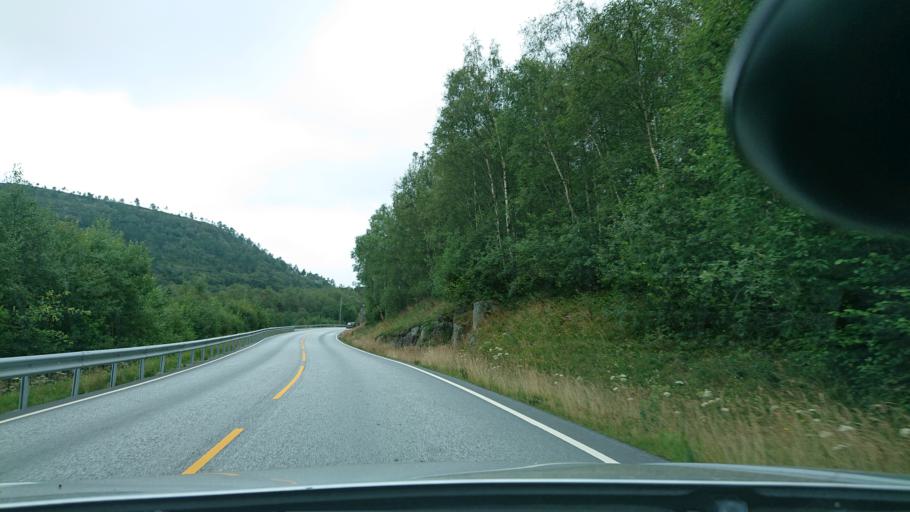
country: NO
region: Rogaland
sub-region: Hjelmeland
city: Hjelmelandsvagen
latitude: 59.1690
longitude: 6.1580
